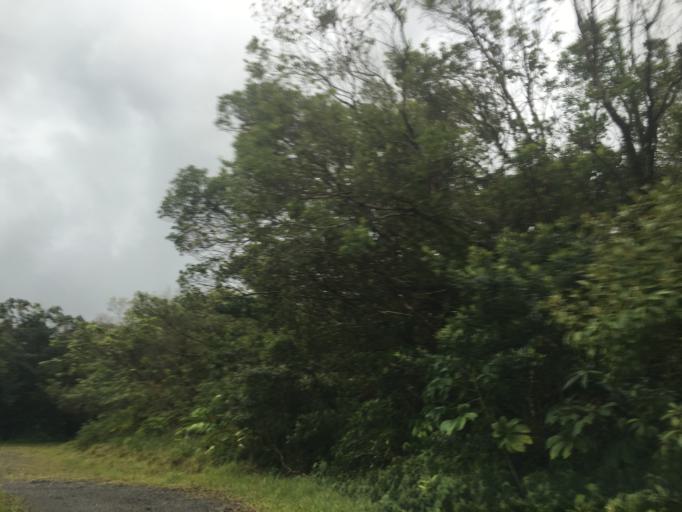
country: CR
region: Alajuela
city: La Fortuna
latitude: 10.4611
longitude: -84.7281
